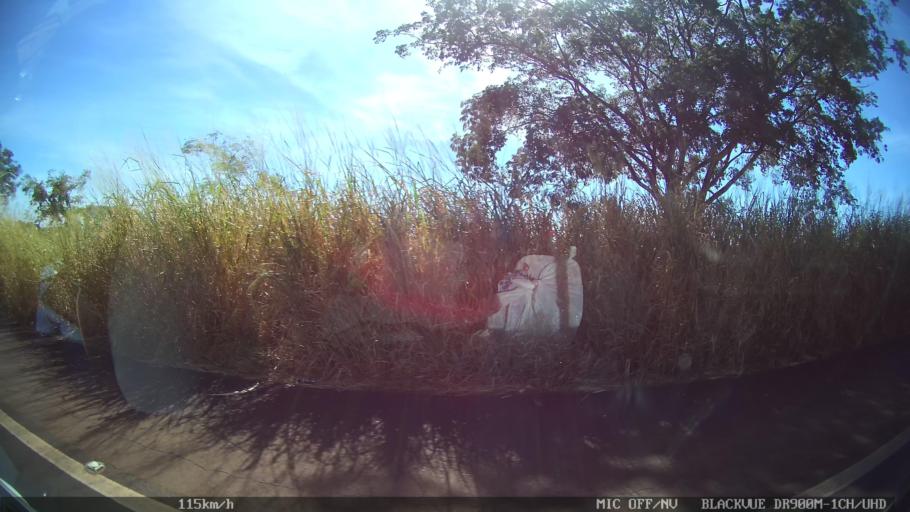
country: BR
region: Sao Paulo
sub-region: Franca
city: Franca
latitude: -20.5615
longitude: -47.6153
